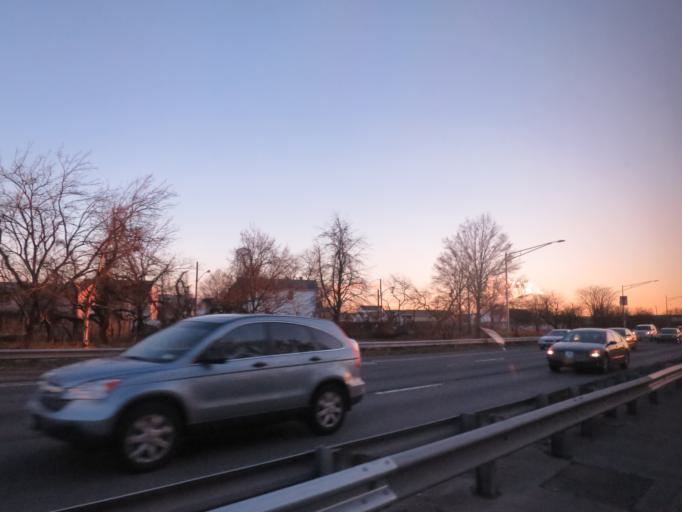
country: US
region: New York
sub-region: Queens County
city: Borough of Queens
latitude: 40.6599
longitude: -73.8536
